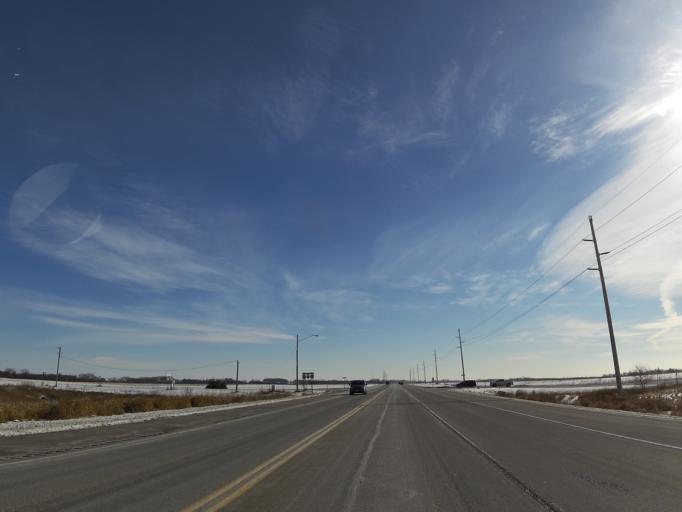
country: US
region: Minnesota
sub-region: Washington County
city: Cottage Grove
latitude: 44.7410
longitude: -92.9511
